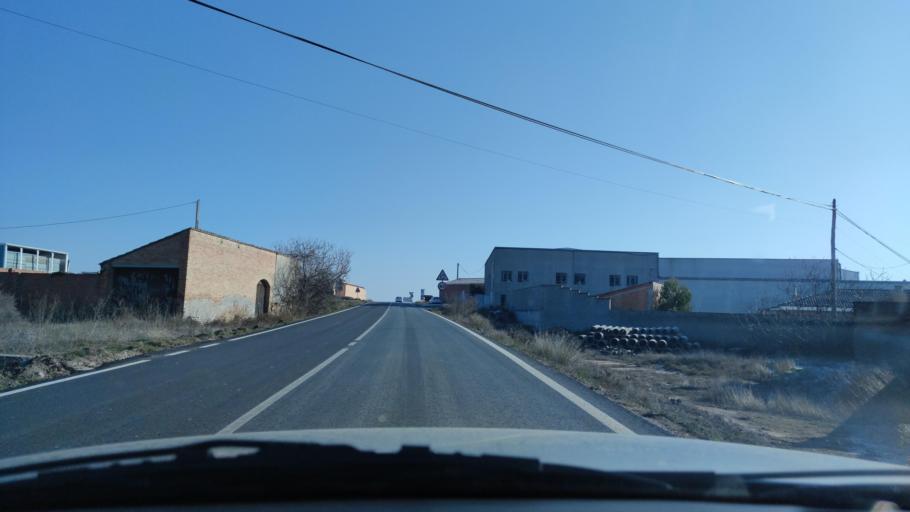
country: ES
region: Catalonia
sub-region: Provincia de Lleida
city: Torrefarrera
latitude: 41.6991
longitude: 0.6298
